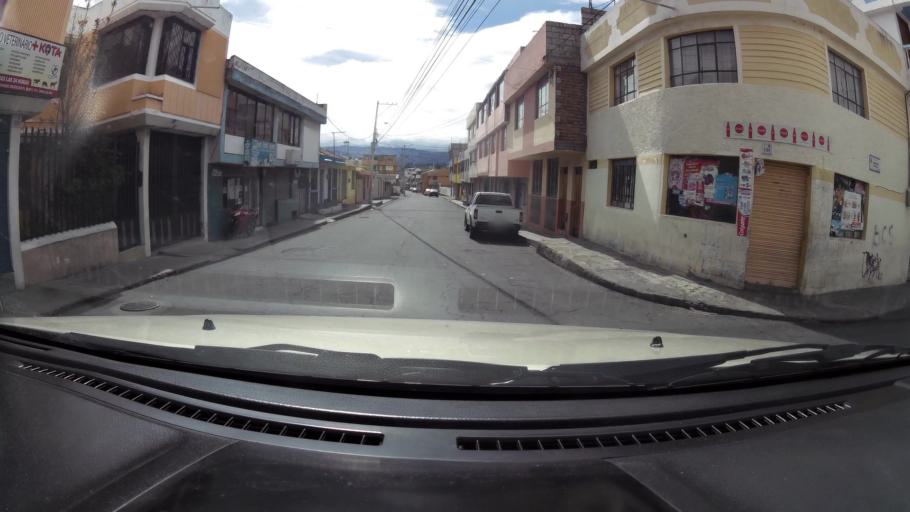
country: EC
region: Cotopaxi
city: Latacunga
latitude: -0.9278
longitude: -78.6219
